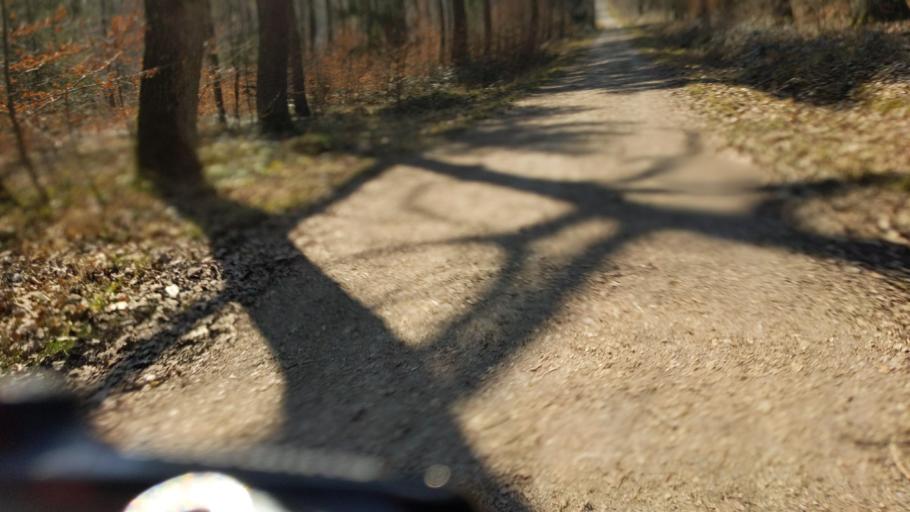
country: DE
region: Baden-Wuerttemberg
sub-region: Regierungsbezirk Stuttgart
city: Gerlingen
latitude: 48.7777
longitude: 9.0963
